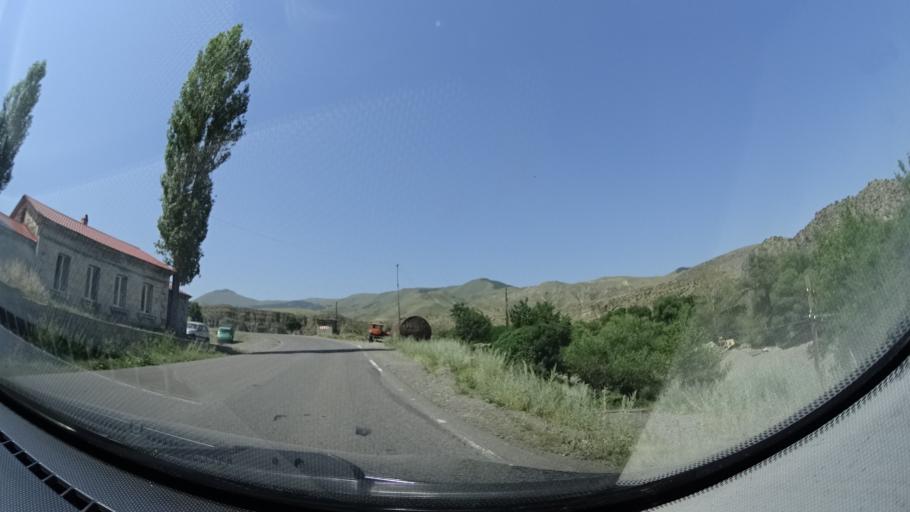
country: GE
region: Samtskhe-Javakheti
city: Aspindza
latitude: 41.5396
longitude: 43.2605
